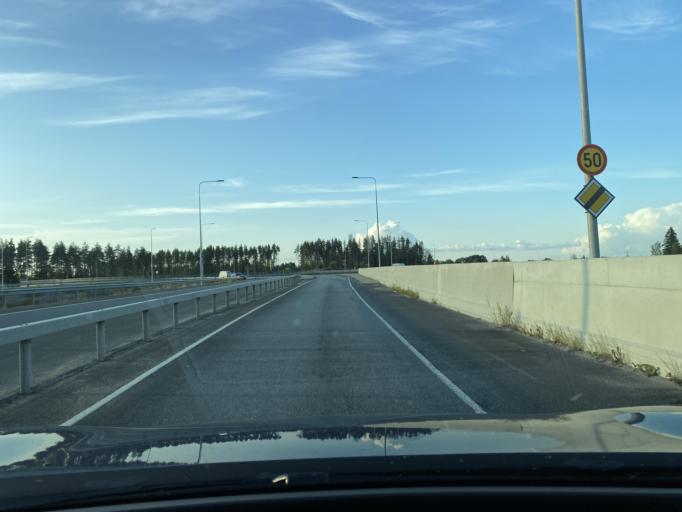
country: FI
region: Southern Ostrobothnia
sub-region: Seinaejoki
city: Nurmo
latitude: 62.8200
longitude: 22.9139
